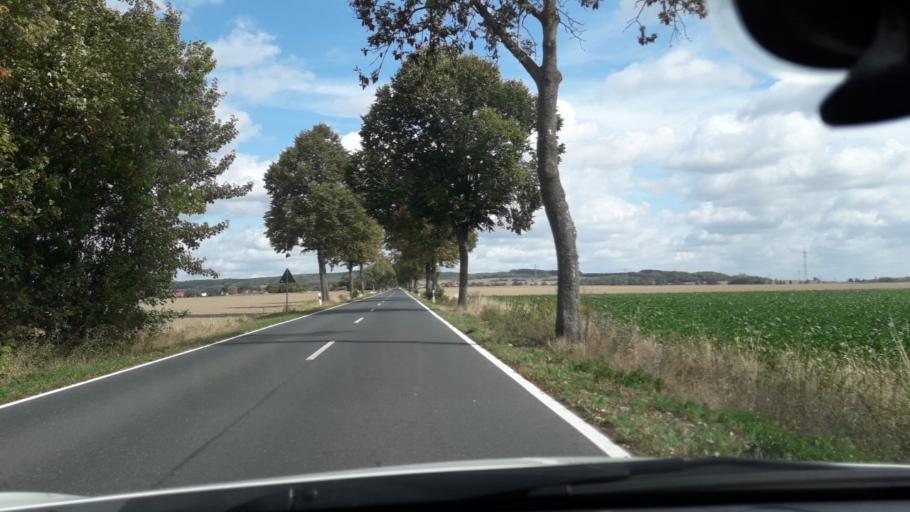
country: DE
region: Lower Saxony
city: Alt Wallmoden
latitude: 52.0433
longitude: 10.3115
